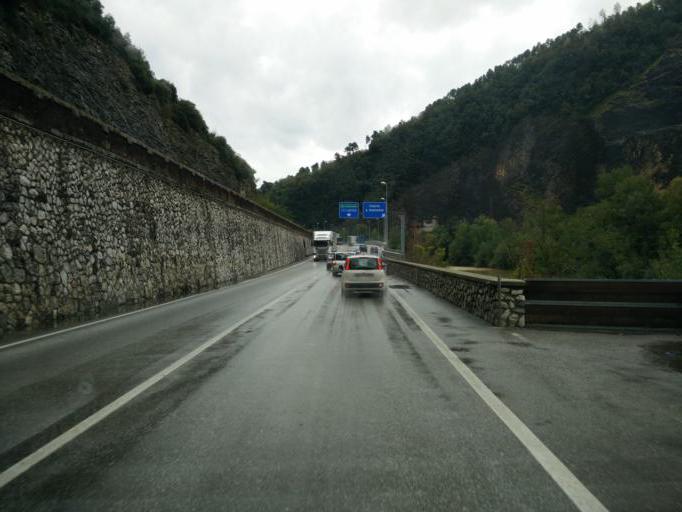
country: IT
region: Tuscany
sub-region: Provincia di Lucca
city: Valdottavo
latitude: 43.9284
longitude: 10.5159
